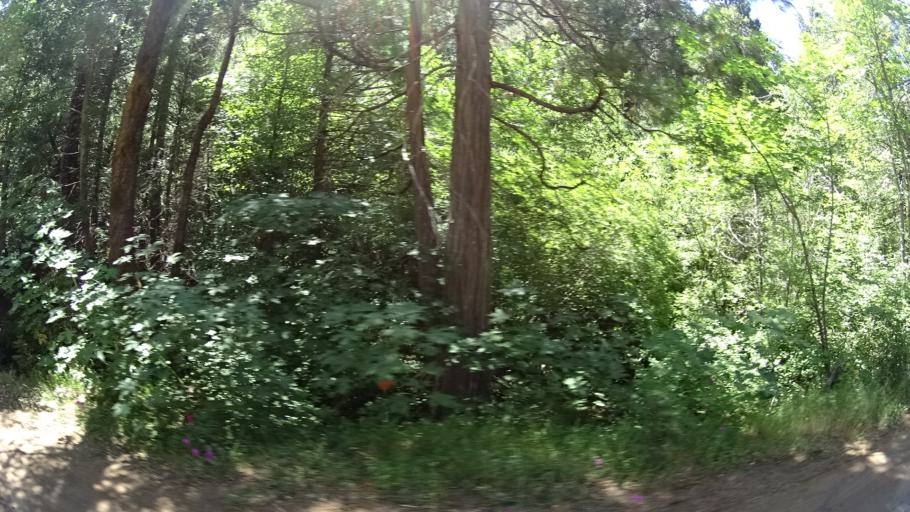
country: US
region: California
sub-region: Calaveras County
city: Arnold
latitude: 38.2191
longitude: -120.3440
